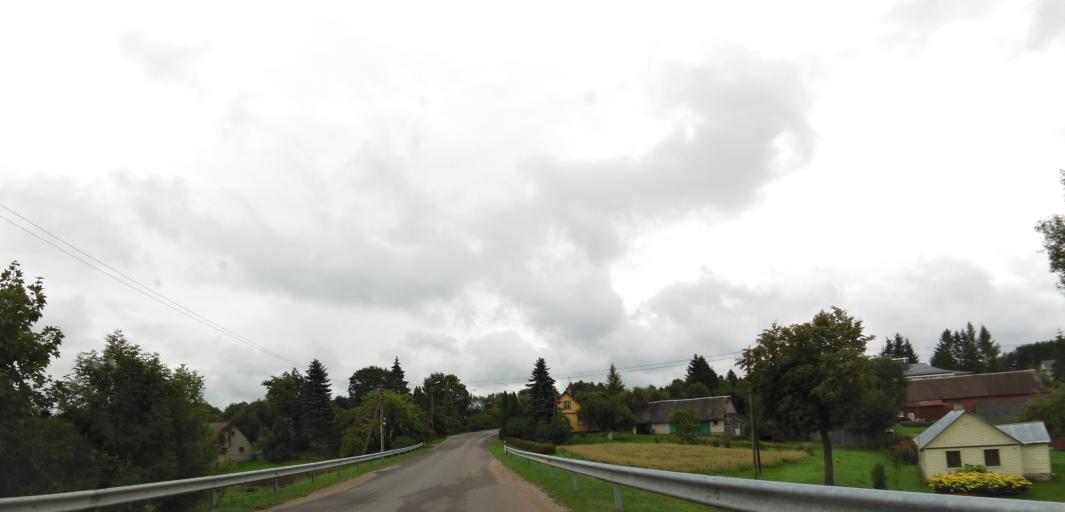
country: LT
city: Sirvintos
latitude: 55.2222
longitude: 25.0939
